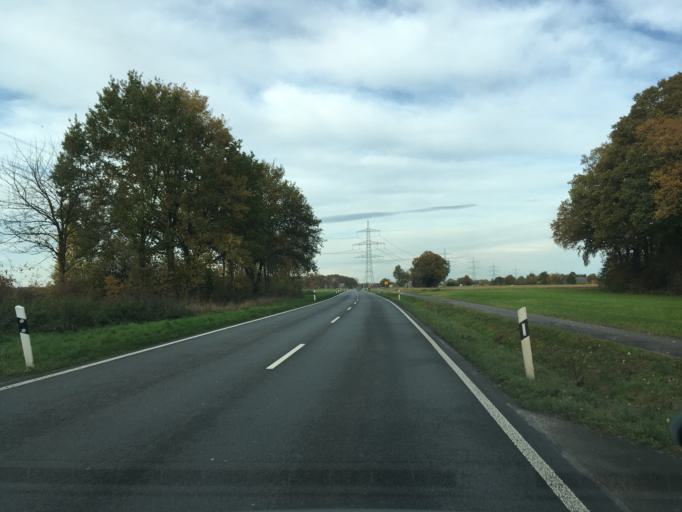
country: DE
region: North Rhine-Westphalia
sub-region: Regierungsbezirk Munster
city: Heiden
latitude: 51.8861
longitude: 6.9047
